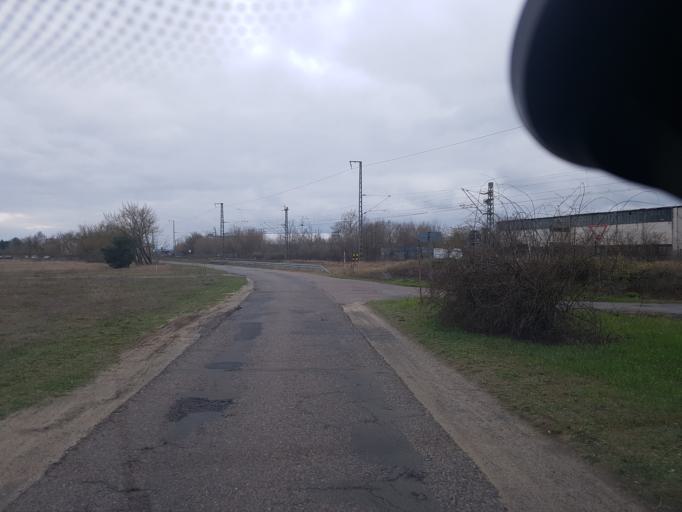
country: DE
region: Brandenburg
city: Eisenhuettenstadt
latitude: 52.1539
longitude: 14.6594
